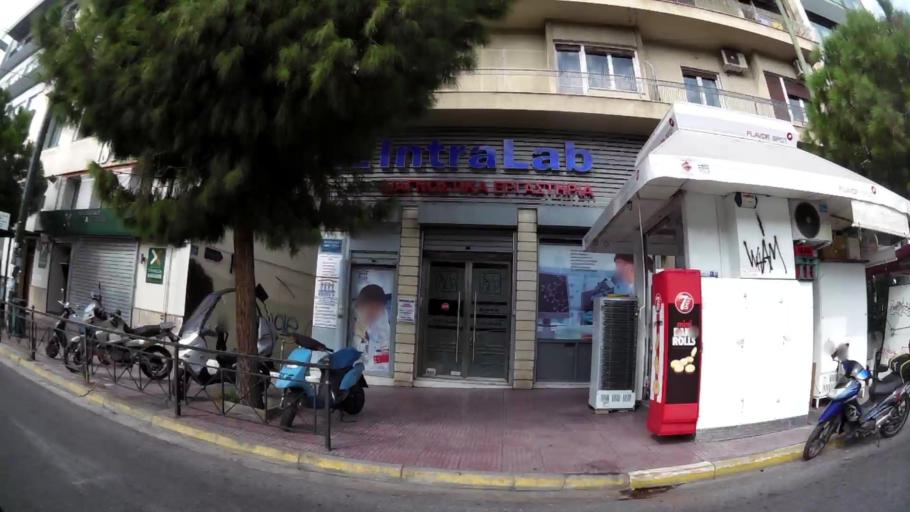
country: GR
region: Attica
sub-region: Nomarchia Athinas
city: Dhafni
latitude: 37.9650
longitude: 23.7271
